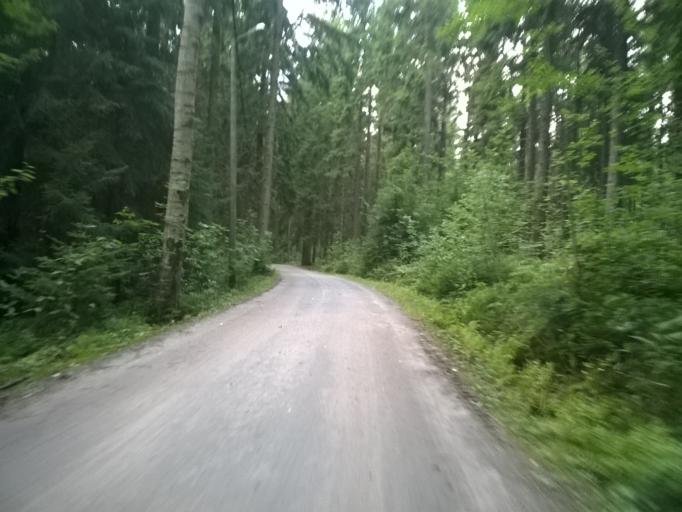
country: FI
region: Uusimaa
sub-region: Helsinki
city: Helsinki
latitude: 60.2660
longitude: 24.9054
